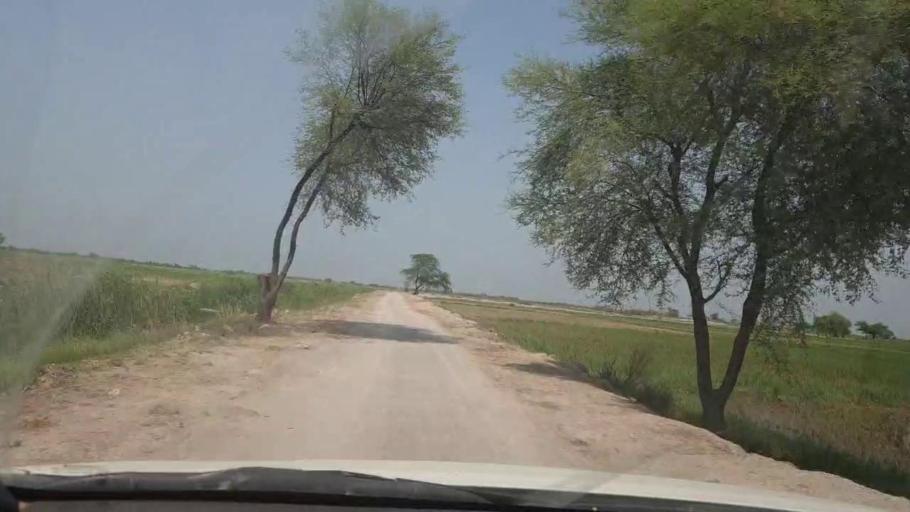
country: PK
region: Sindh
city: Lakhi
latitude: 27.8813
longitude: 68.7366
